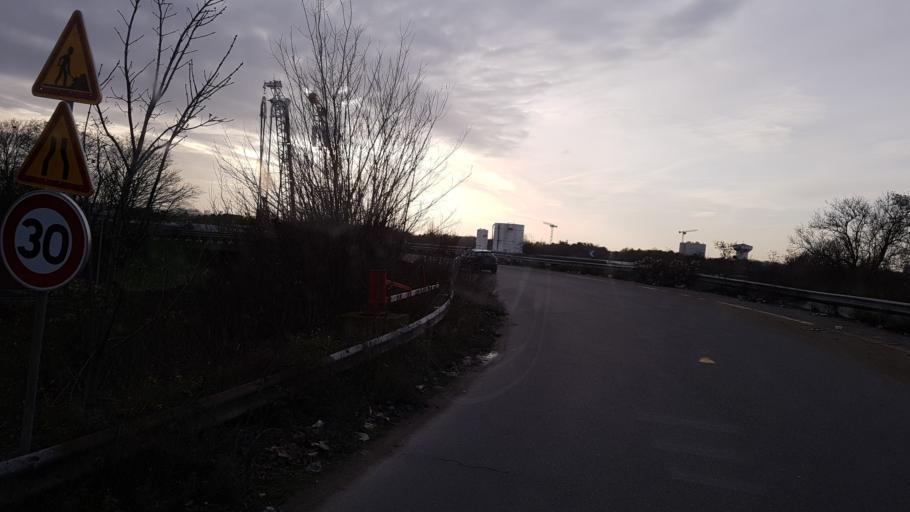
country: FR
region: Ile-de-France
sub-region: Departement de Seine-Saint-Denis
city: Le Blanc-Mesnil
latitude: 48.9507
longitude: 2.4728
